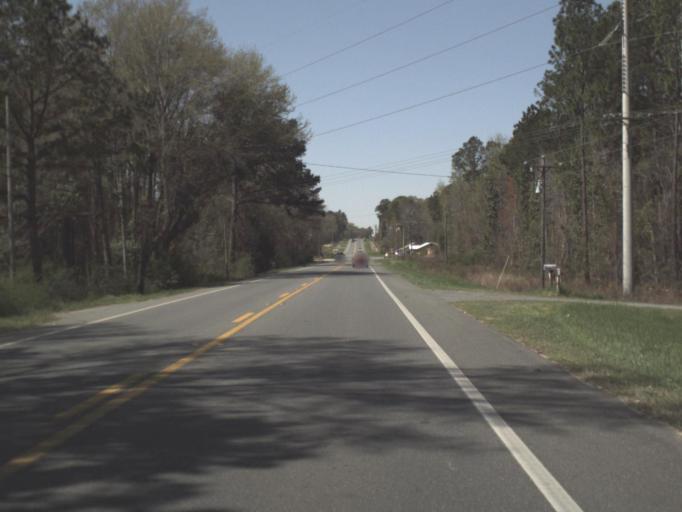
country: US
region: Florida
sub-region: Jackson County
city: Graceville
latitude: 30.9643
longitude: -85.5341
